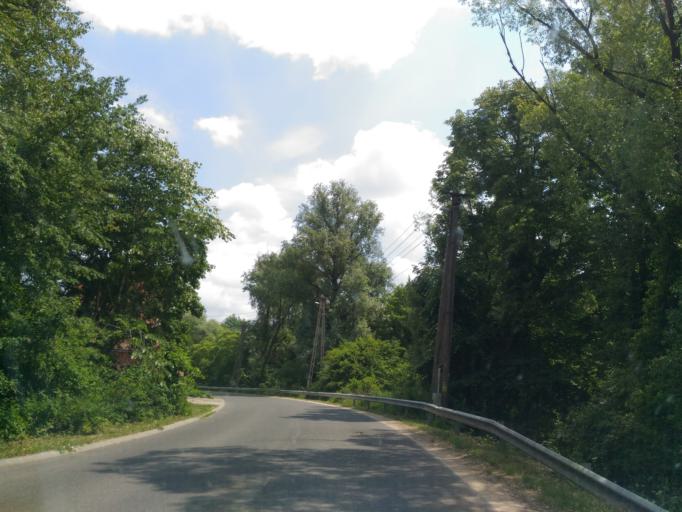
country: HU
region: Baranya
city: Komlo
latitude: 46.1750
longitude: 18.2234
